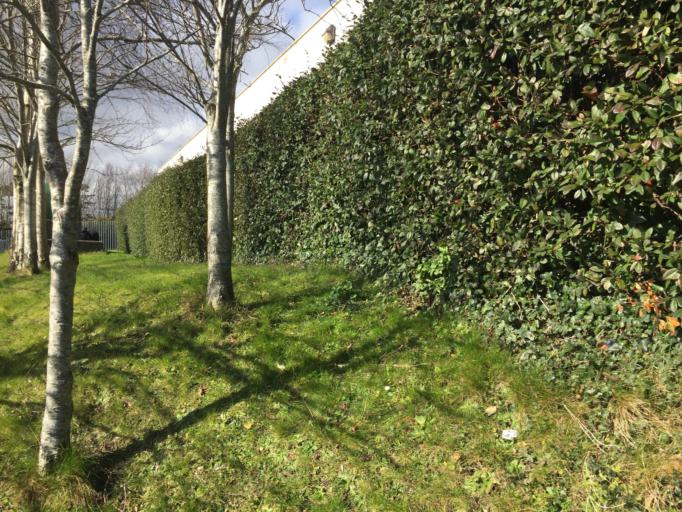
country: IE
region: Leinster
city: Portmarnock
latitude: 53.4321
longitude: -6.1374
